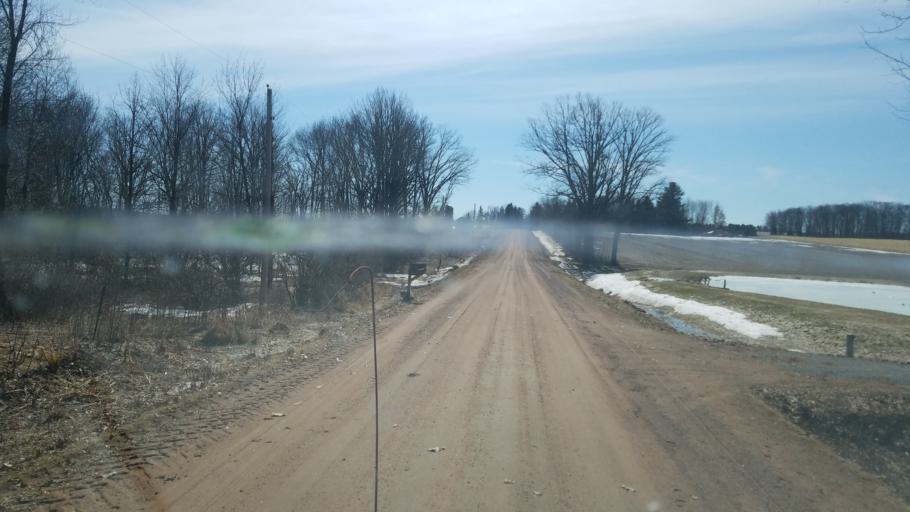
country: US
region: Wisconsin
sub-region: Clark County
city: Loyal
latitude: 44.6298
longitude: -90.4072
